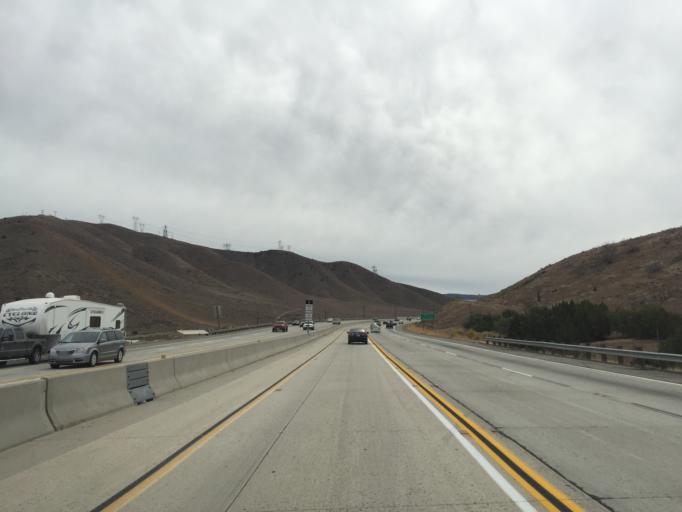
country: US
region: California
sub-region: Los Angeles County
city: Vincent
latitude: 34.5155
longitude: -118.1107
